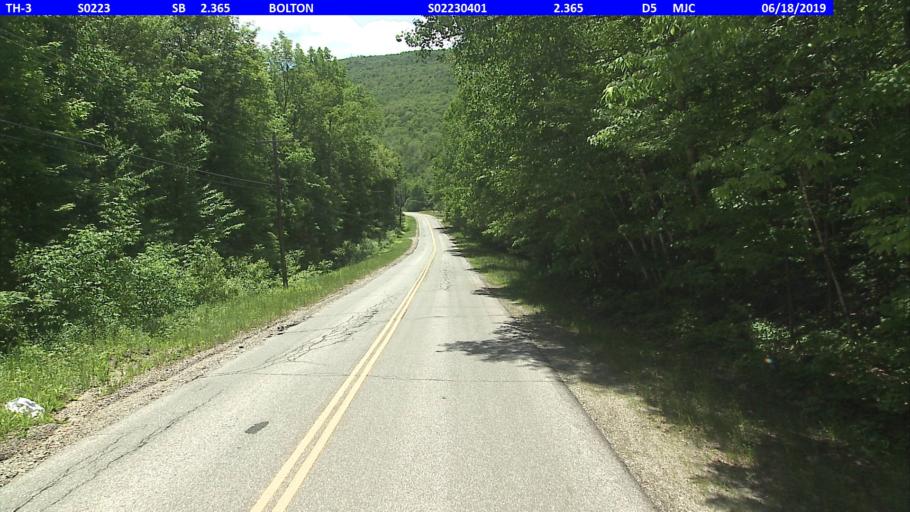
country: US
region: Vermont
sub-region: Washington County
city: Waterbury
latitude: 44.4023
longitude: -72.8759
